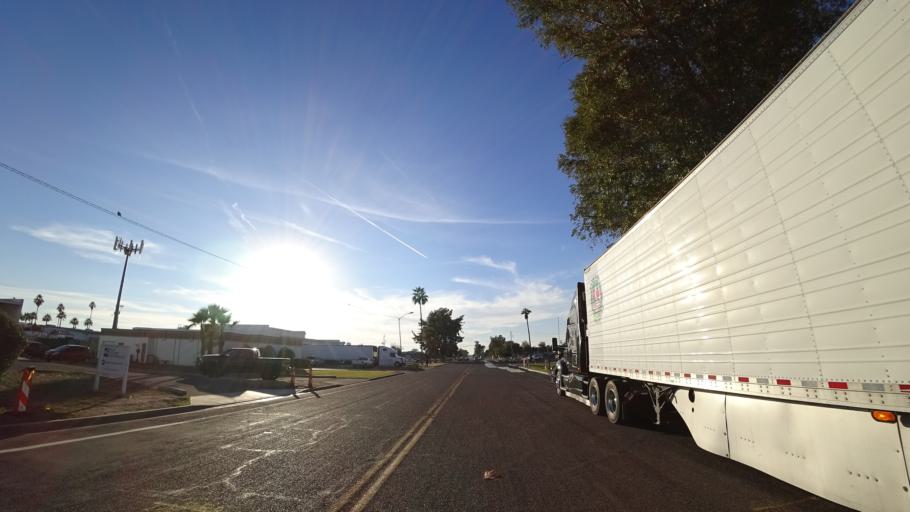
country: US
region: Arizona
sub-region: Maricopa County
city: Phoenix
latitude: 33.4240
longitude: -112.0284
